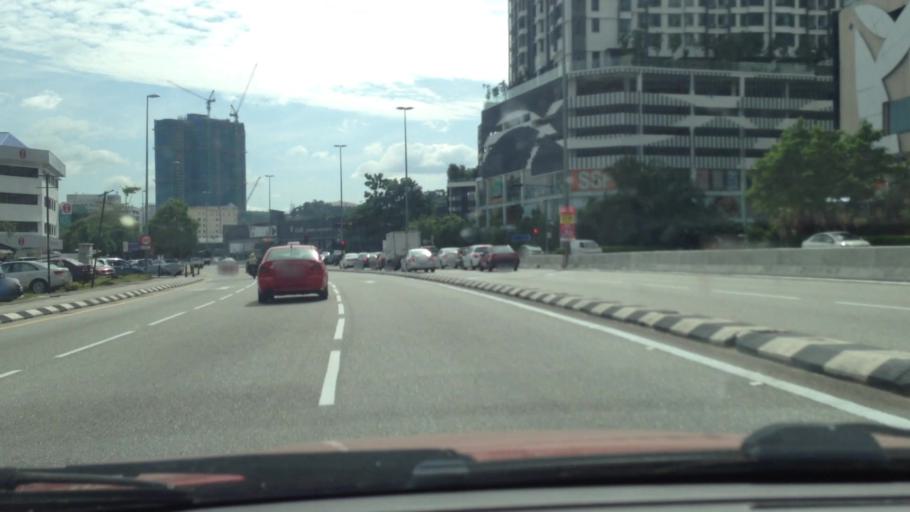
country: MY
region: Kuala Lumpur
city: Kuala Lumpur
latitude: 3.0850
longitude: 101.6728
